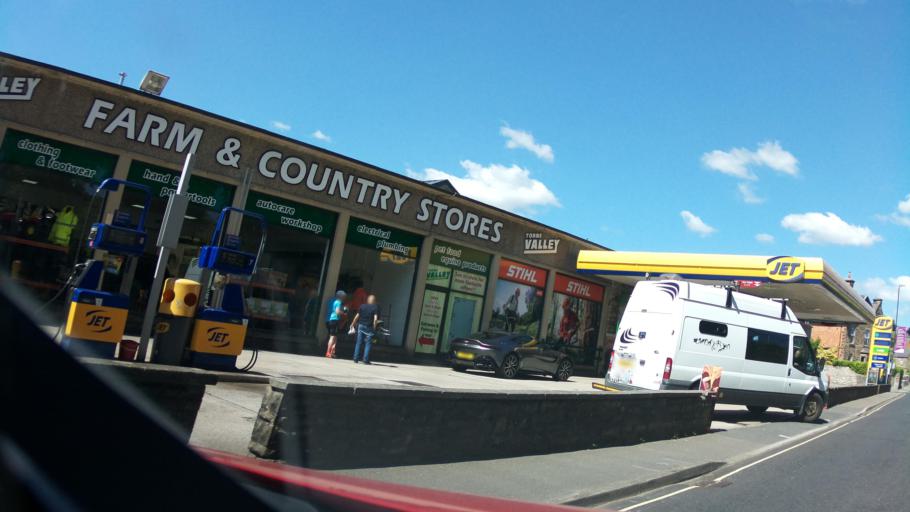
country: GB
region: England
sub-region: Derbyshire
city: Bakewell
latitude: 53.2099
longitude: -1.6723
